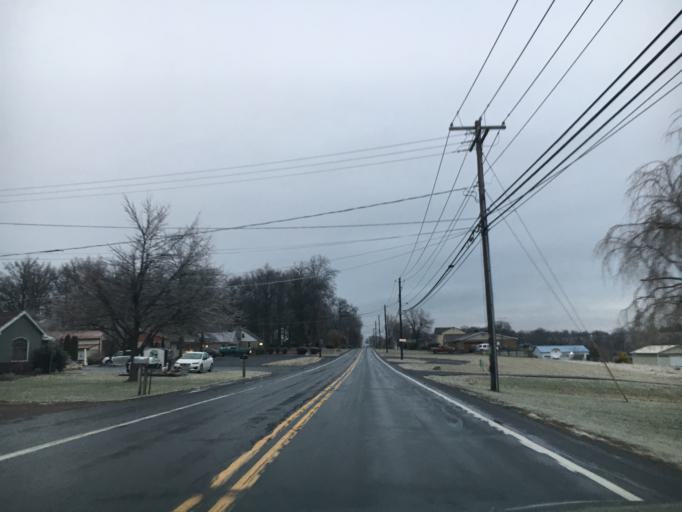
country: US
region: Pennsylvania
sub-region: Lehigh County
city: Schnecksville
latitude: 40.6162
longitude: -75.6440
